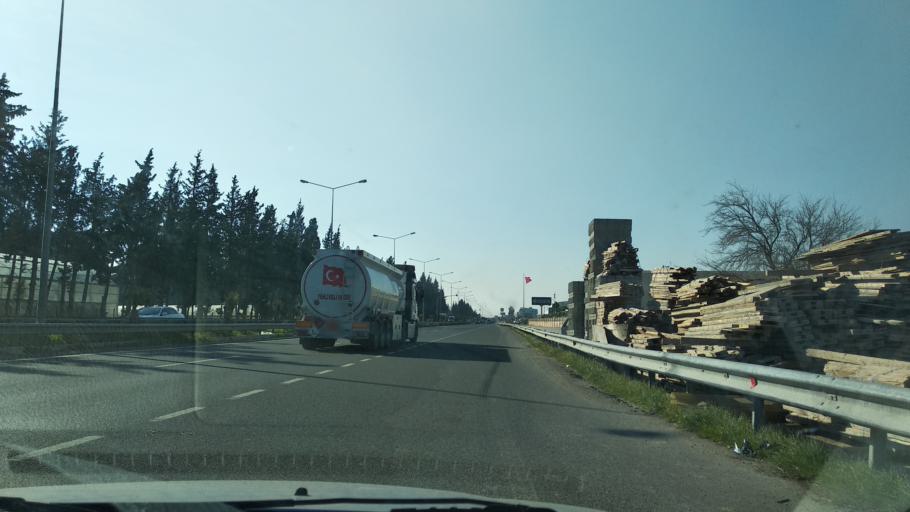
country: TR
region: Izmir
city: Menemen
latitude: 38.5694
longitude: 27.0550
